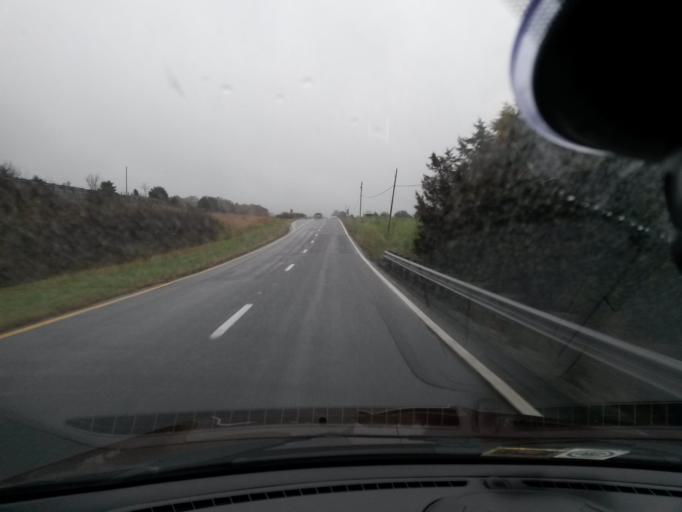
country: US
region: Virginia
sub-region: Botetourt County
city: Fincastle
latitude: 37.5739
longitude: -79.8363
